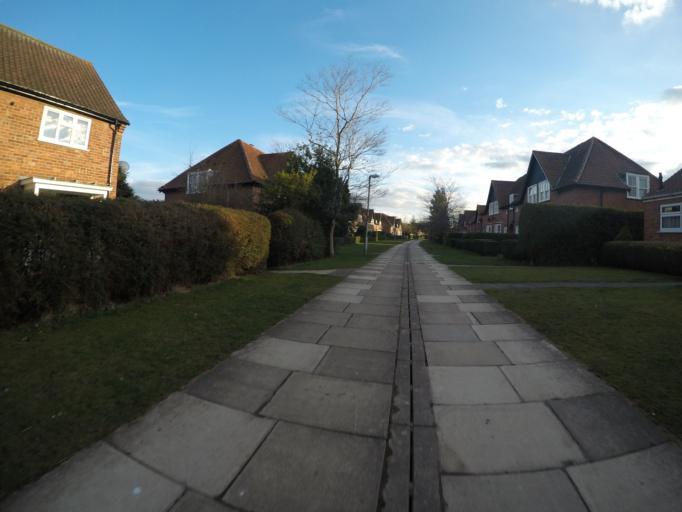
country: GB
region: England
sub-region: City of York
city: Huntington
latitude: 53.9935
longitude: -1.0691
